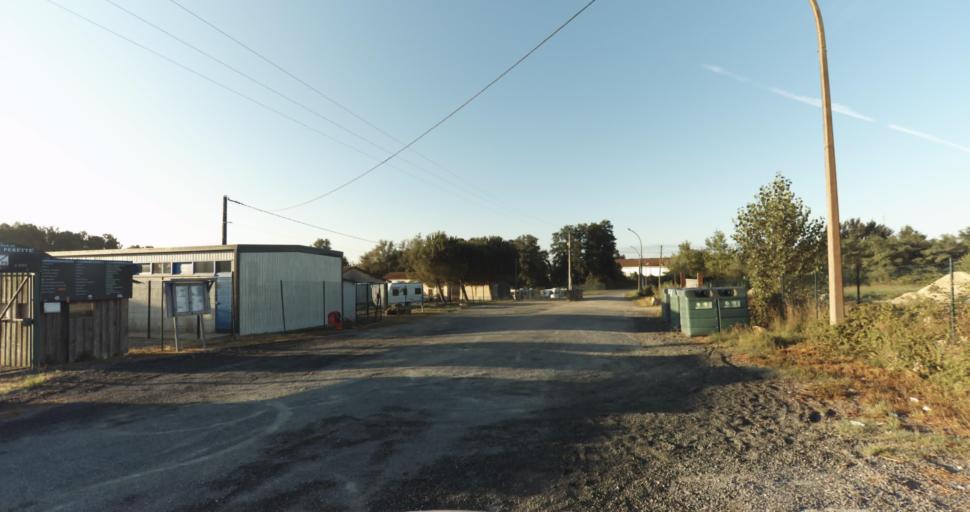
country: FR
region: Aquitaine
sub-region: Departement de la Gironde
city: Bazas
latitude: 44.4413
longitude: -0.2272
